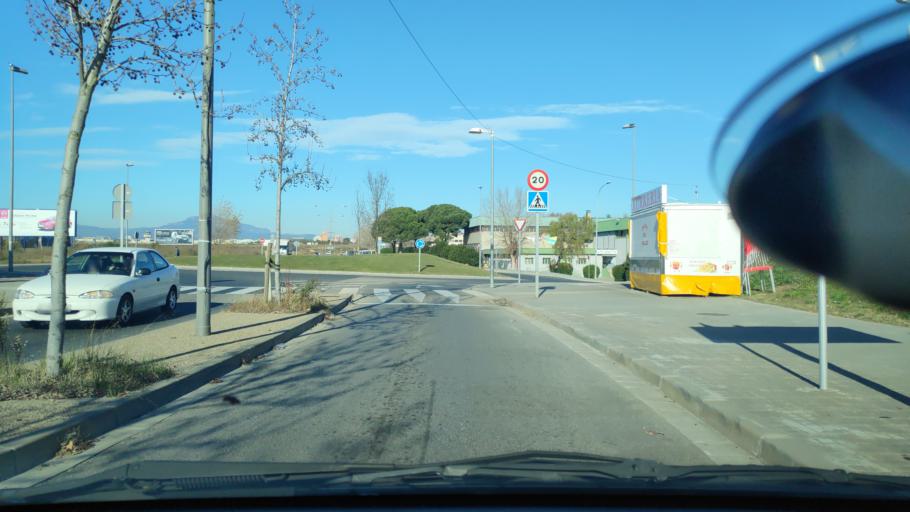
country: ES
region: Catalonia
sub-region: Provincia de Barcelona
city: Barbera del Valles
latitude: 41.5135
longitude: 2.1132
